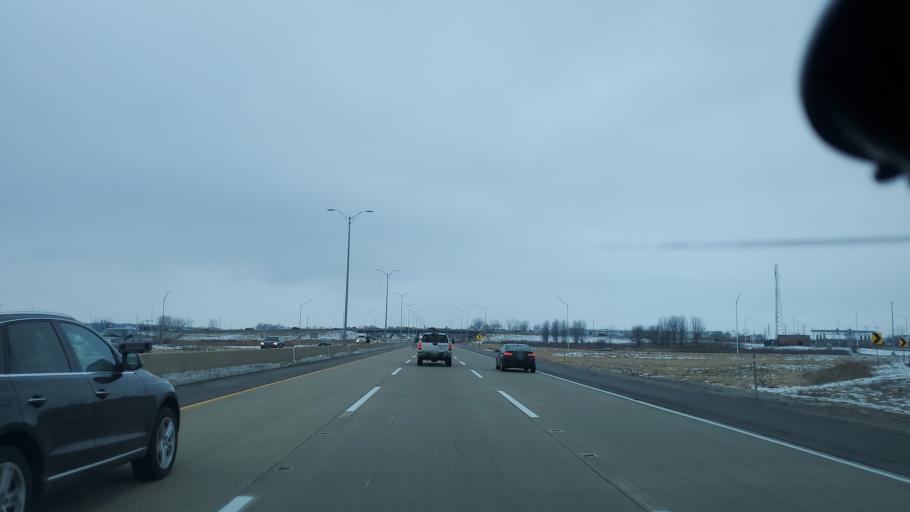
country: US
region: Illinois
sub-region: Kane County
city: North Aurora
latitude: 41.7951
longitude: -88.3700
